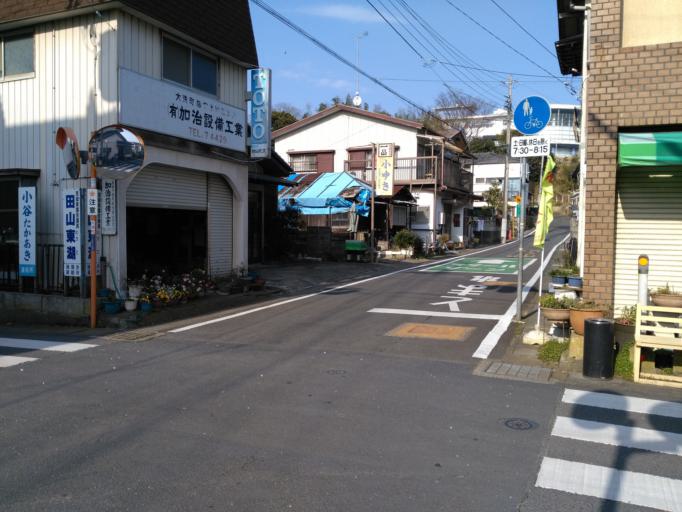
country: JP
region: Ibaraki
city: Oarai
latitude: 36.3159
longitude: 140.5737
